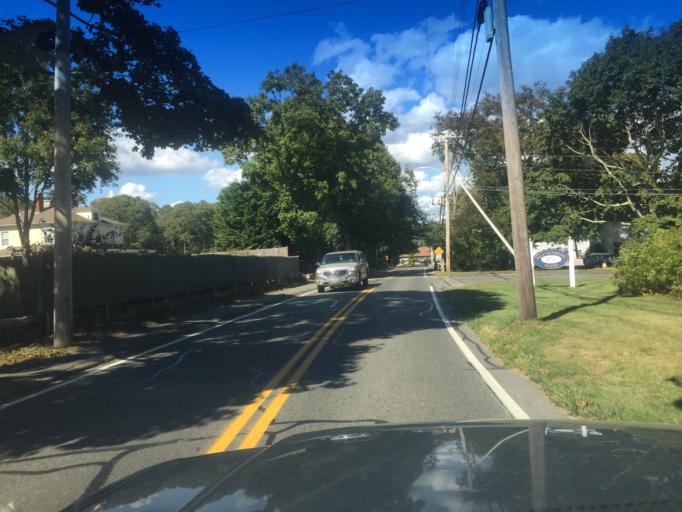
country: US
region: Massachusetts
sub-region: Barnstable County
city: Pocasset
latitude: 41.6915
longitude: -70.6194
